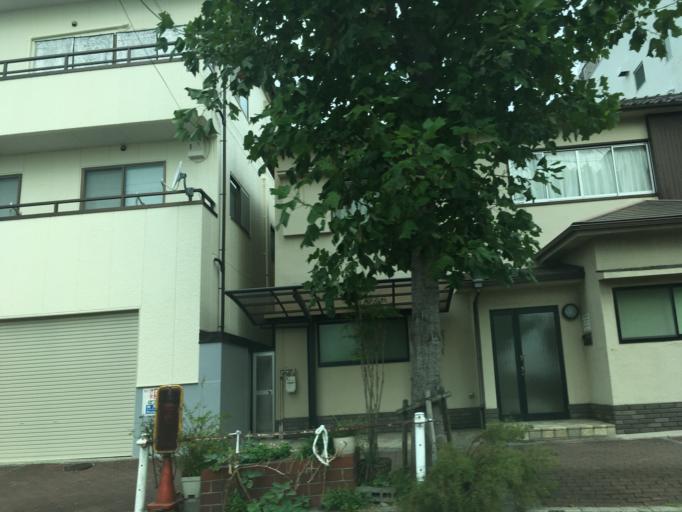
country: JP
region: Hyogo
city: Kobe
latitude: 34.7082
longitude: 135.2102
